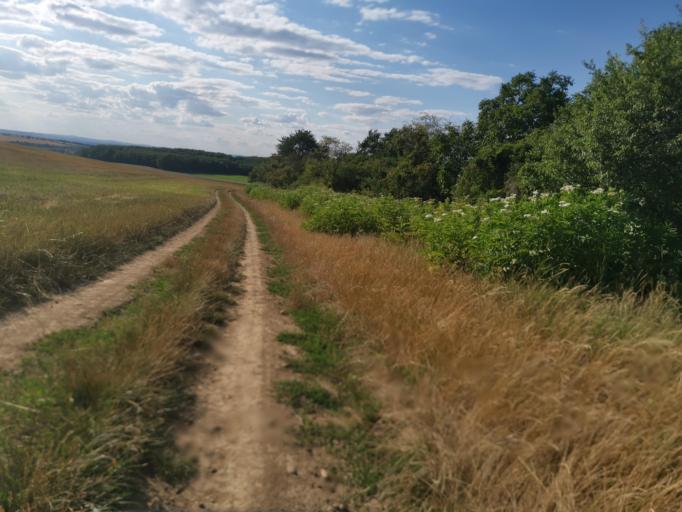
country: CZ
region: South Moravian
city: Sudomerice
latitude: 48.8159
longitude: 17.2806
